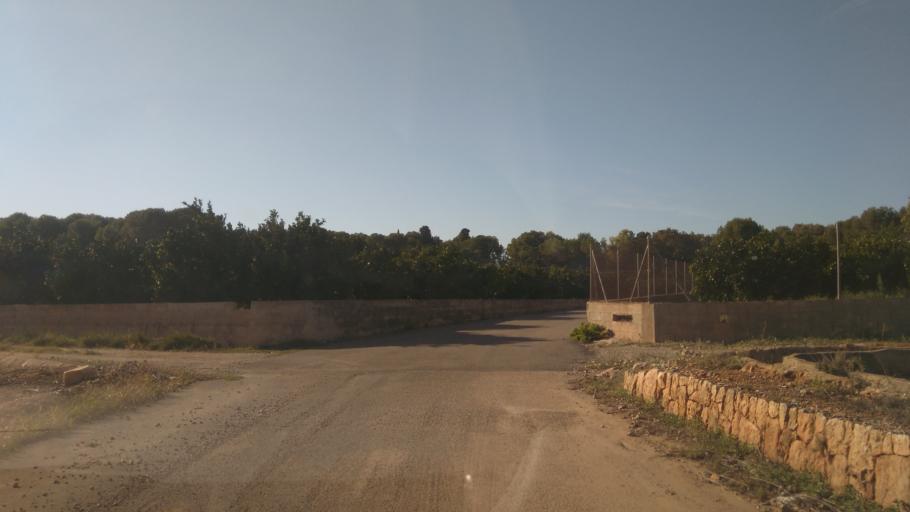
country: ES
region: Valencia
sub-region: Provincia de Valencia
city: Benimodo
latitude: 39.1766
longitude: -0.5564
